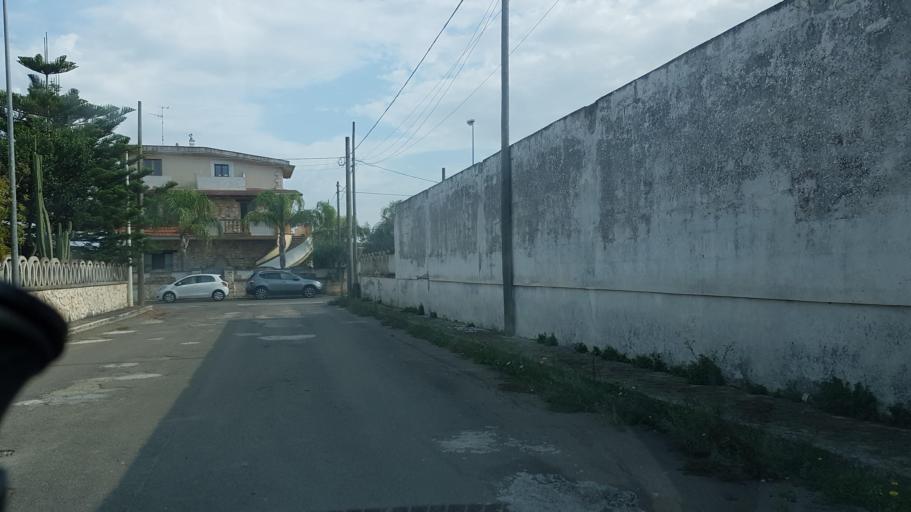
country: IT
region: Apulia
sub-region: Provincia di Brindisi
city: Cellino San Marco
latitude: 40.4790
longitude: 17.9753
